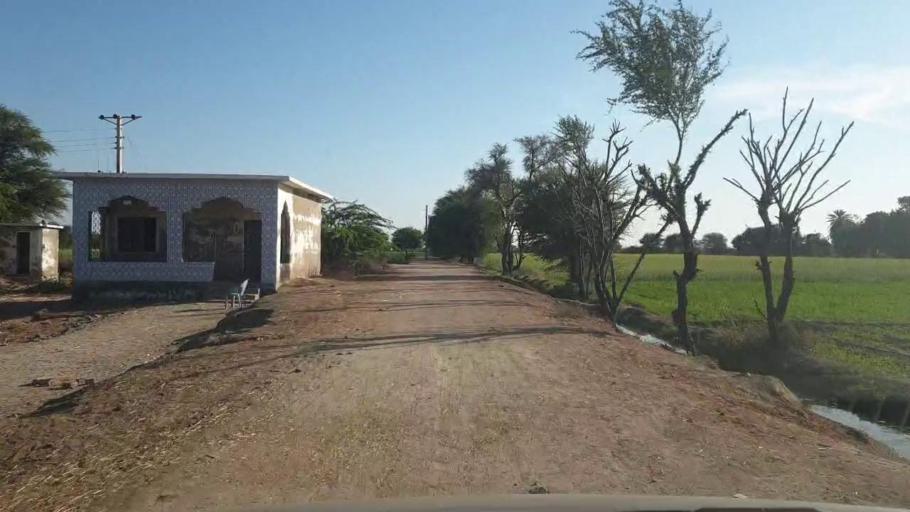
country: PK
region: Sindh
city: Dhoro Naro
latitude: 25.4293
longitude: 69.5388
